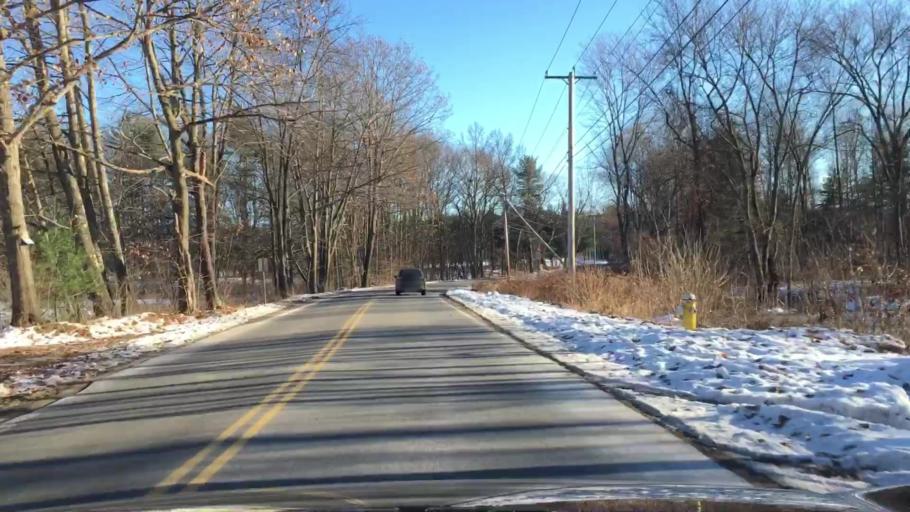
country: US
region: New Hampshire
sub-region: Hillsborough County
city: Milford
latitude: 42.8266
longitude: -71.5844
